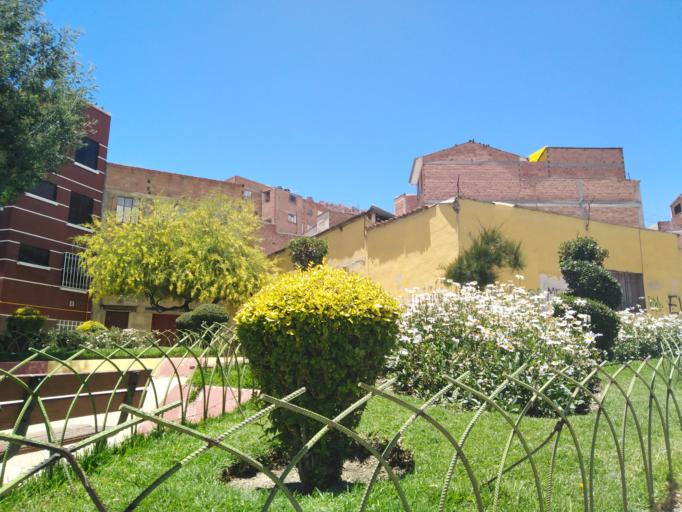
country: BO
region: La Paz
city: La Paz
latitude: -16.5140
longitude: -68.1403
